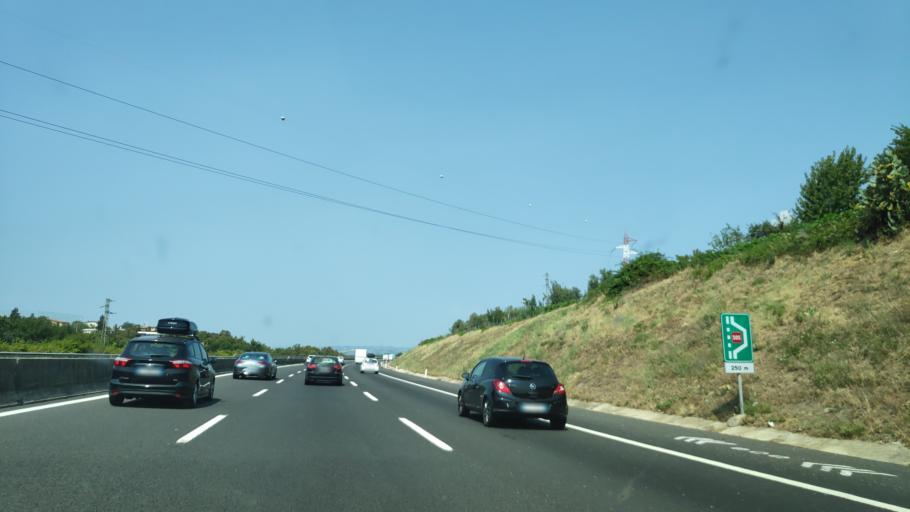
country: IT
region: Latium
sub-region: Citta metropolitana di Roma Capitale
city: Colle Mainello
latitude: 41.8702
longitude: 12.7688
